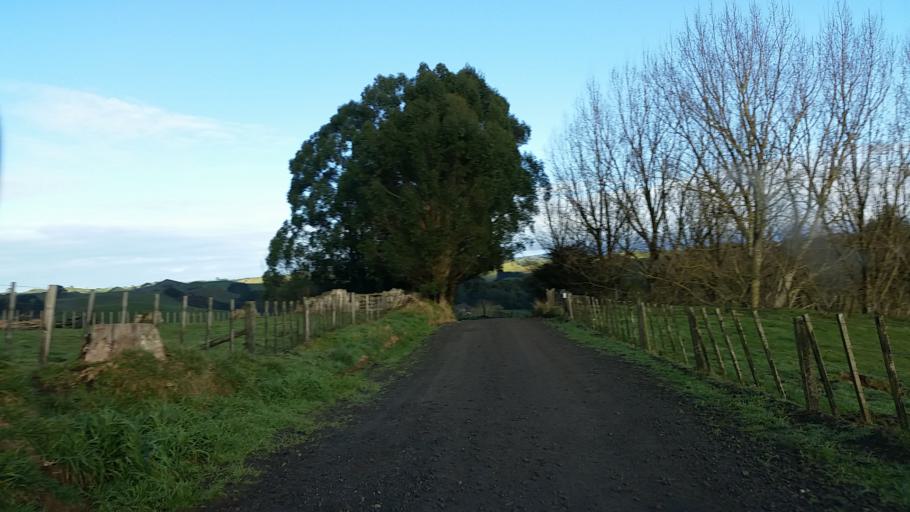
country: NZ
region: Taranaki
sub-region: South Taranaki District
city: Eltham
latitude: -39.2458
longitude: 174.3811
